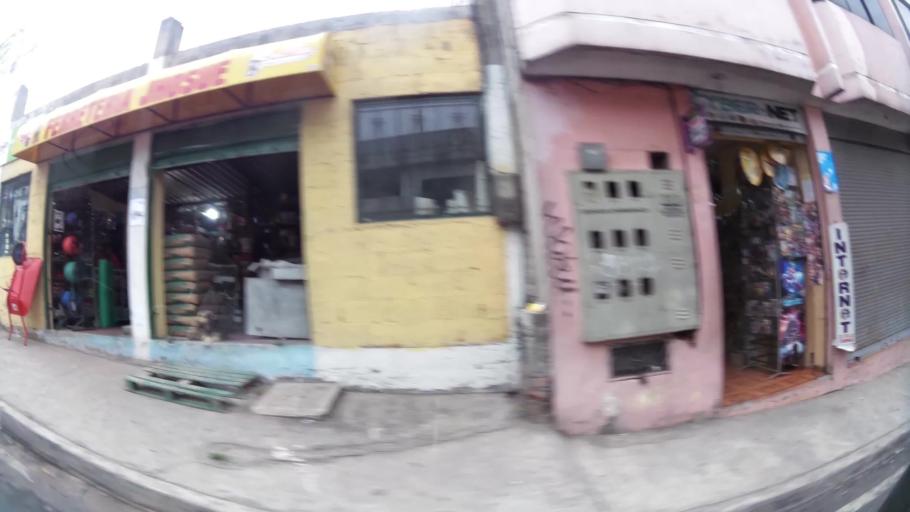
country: EC
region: Pichincha
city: Sangolqui
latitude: -0.3192
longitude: -78.5342
